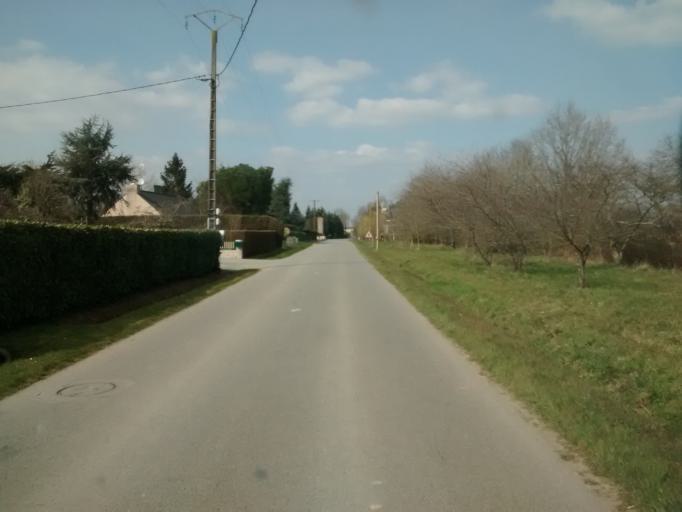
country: FR
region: Brittany
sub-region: Departement d'Ille-et-Vilaine
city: Grand-Fougeray
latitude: 47.7351
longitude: -1.7407
